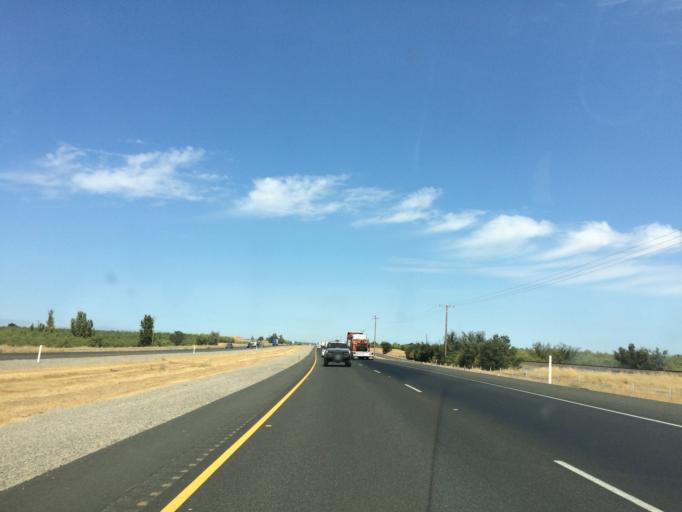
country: US
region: California
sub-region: Colusa County
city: Arbuckle
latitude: 38.9751
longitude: -122.0293
